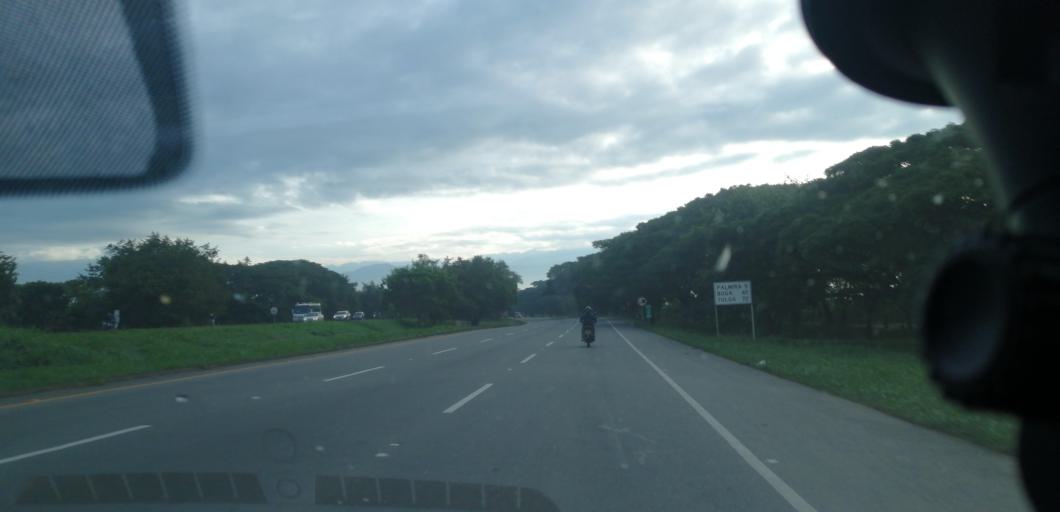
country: CO
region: Valle del Cauca
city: Palmira
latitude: 3.5207
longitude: -76.3555
